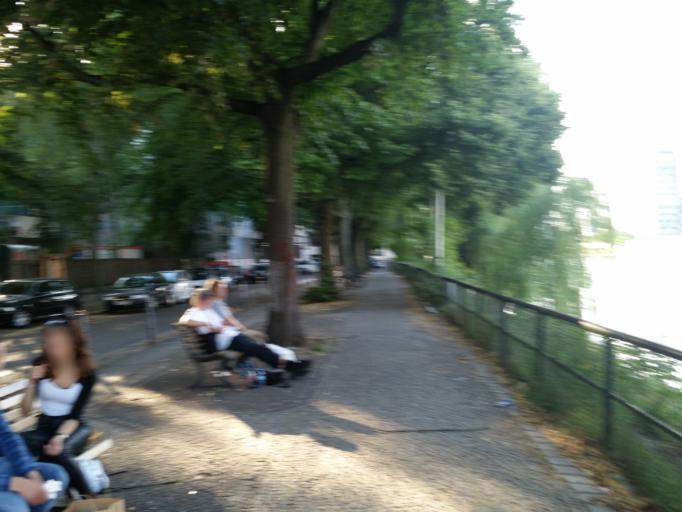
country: DE
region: Berlin
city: Berlin Treptow
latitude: 52.5022
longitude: 13.4426
